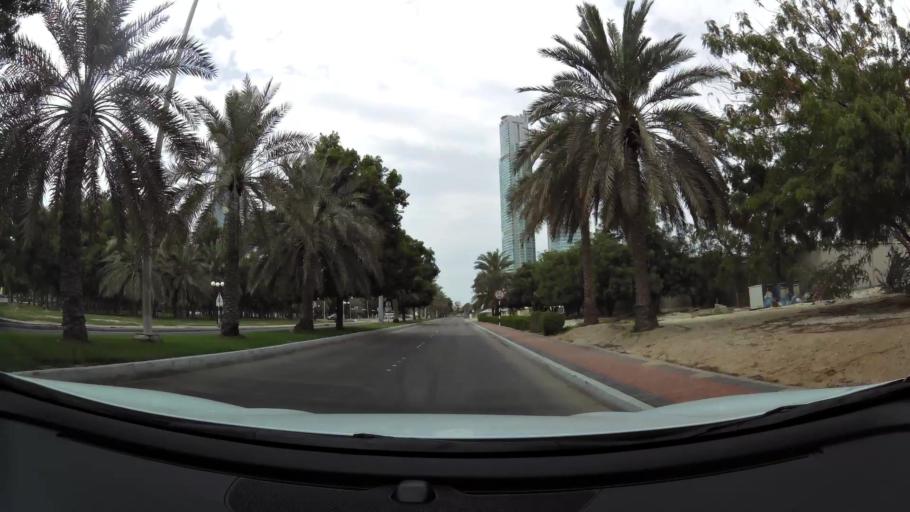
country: AE
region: Abu Dhabi
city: Abu Dhabi
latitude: 24.4596
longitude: 54.3302
